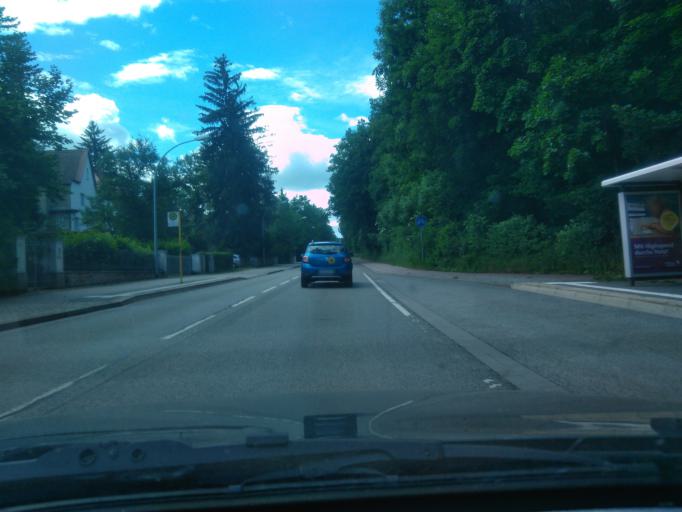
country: DE
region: Thuringia
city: Weimar
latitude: 50.9685
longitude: 11.3239
